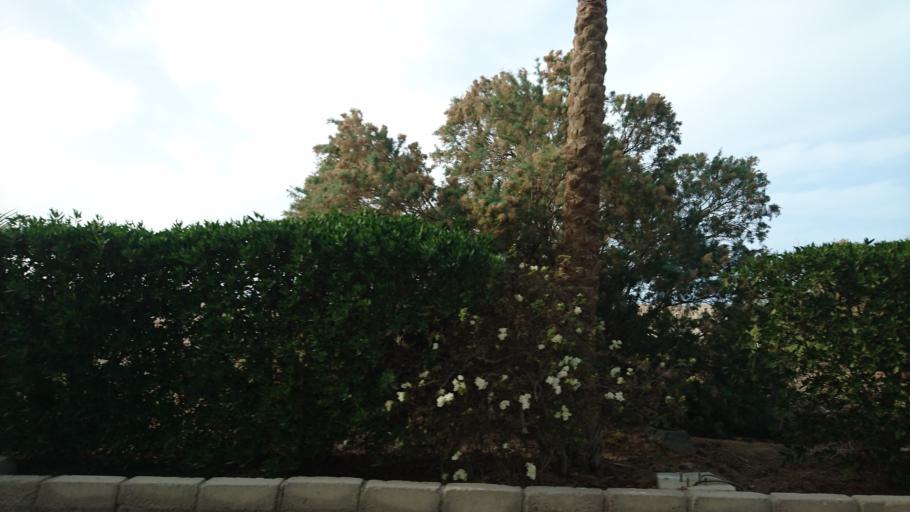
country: EG
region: Red Sea
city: Bur Safajah
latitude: 26.8011
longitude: 33.9397
